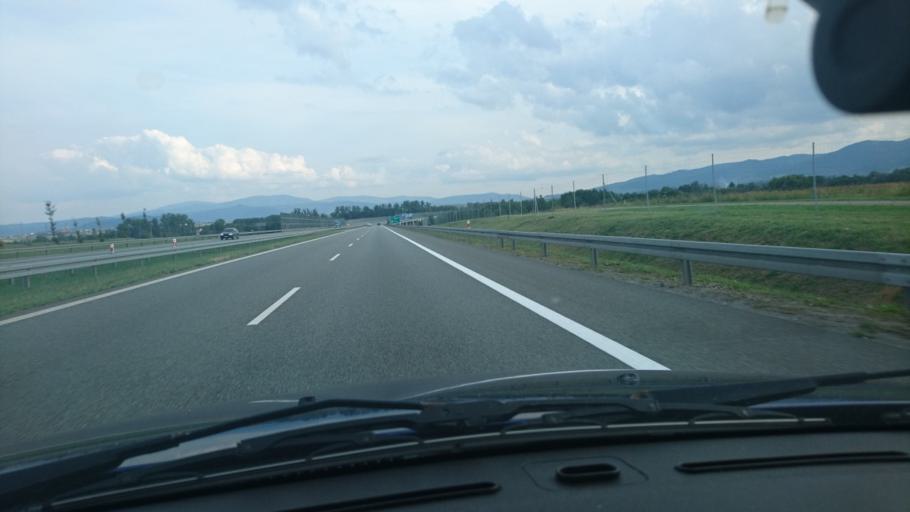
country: PL
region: Silesian Voivodeship
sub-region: Powiat bielski
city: Rybarzowice
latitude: 49.7233
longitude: 19.1199
